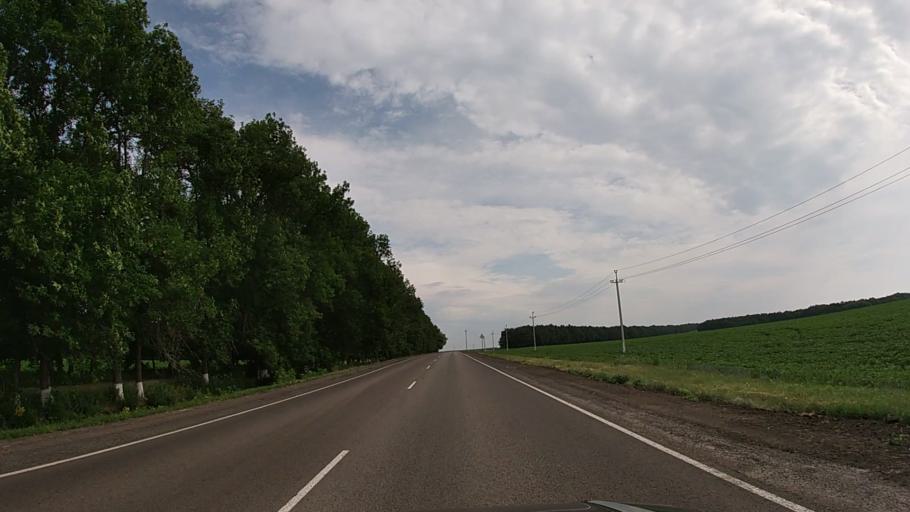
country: RU
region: Belgorod
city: Krasnaya Yaruga
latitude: 50.8116
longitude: 35.5006
